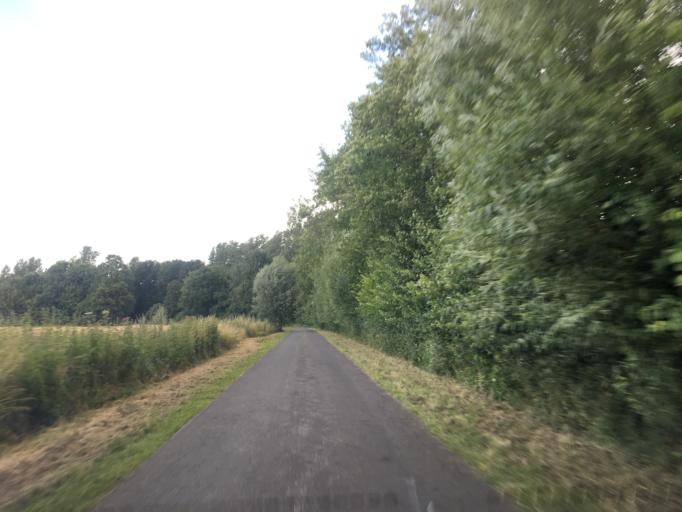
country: DE
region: North Rhine-Westphalia
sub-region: Regierungsbezirk Munster
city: Muenster
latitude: 52.0179
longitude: 7.5893
